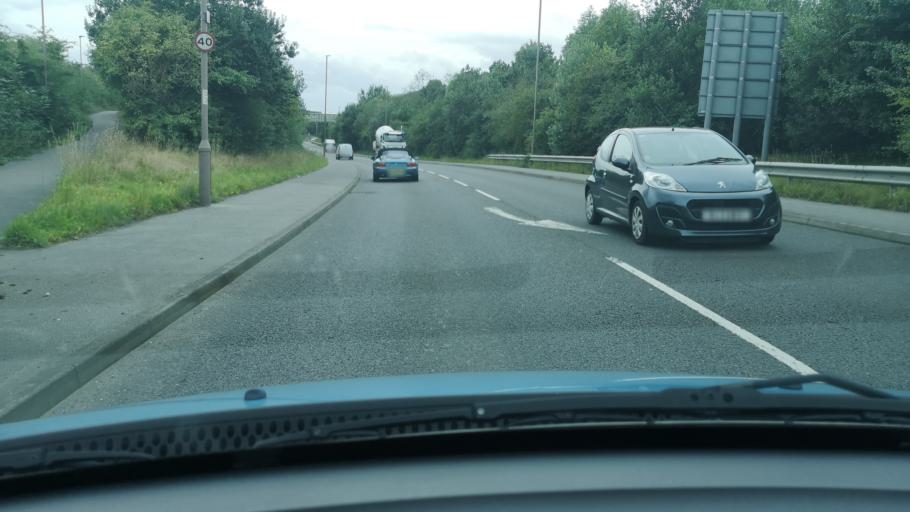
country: GB
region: England
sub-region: Barnsley
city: Shafton
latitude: 53.5900
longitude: -1.4001
